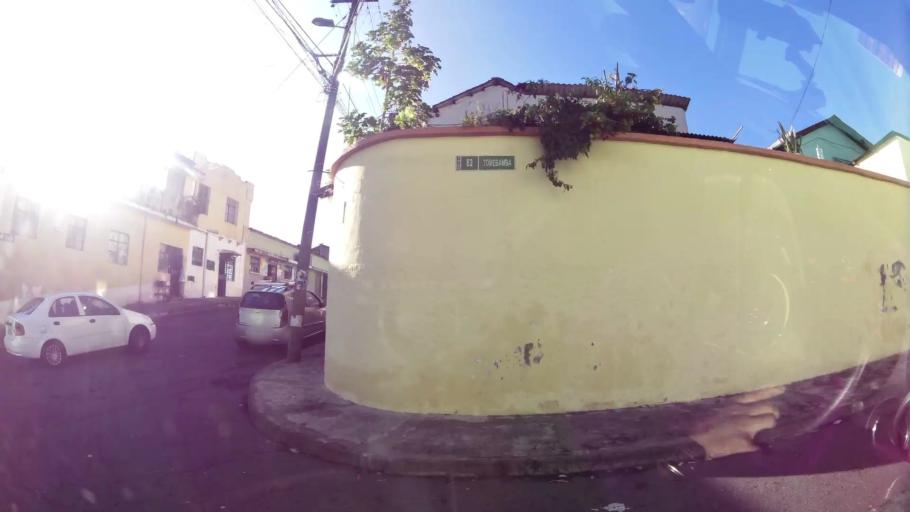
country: EC
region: Pichincha
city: Quito
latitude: -0.2407
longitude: -78.5167
